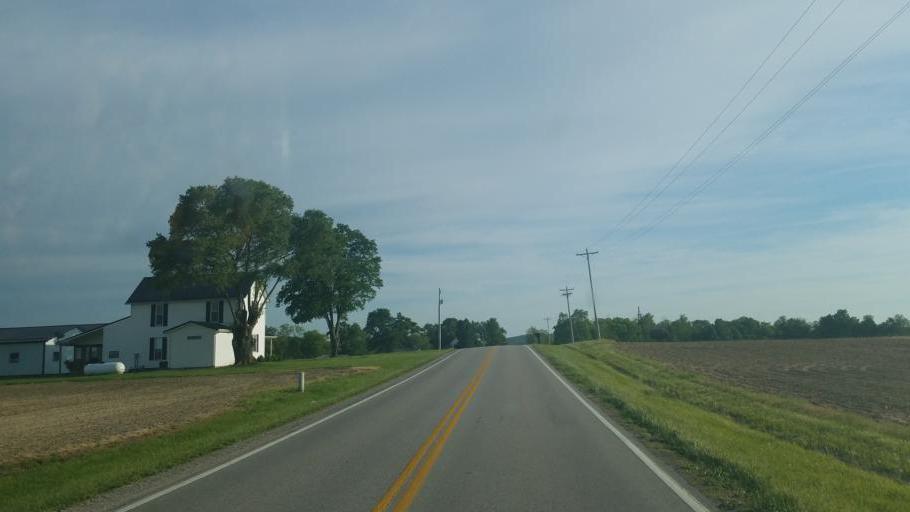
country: US
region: Ohio
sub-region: Ross County
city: Frankfort
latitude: 39.4422
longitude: -83.2200
